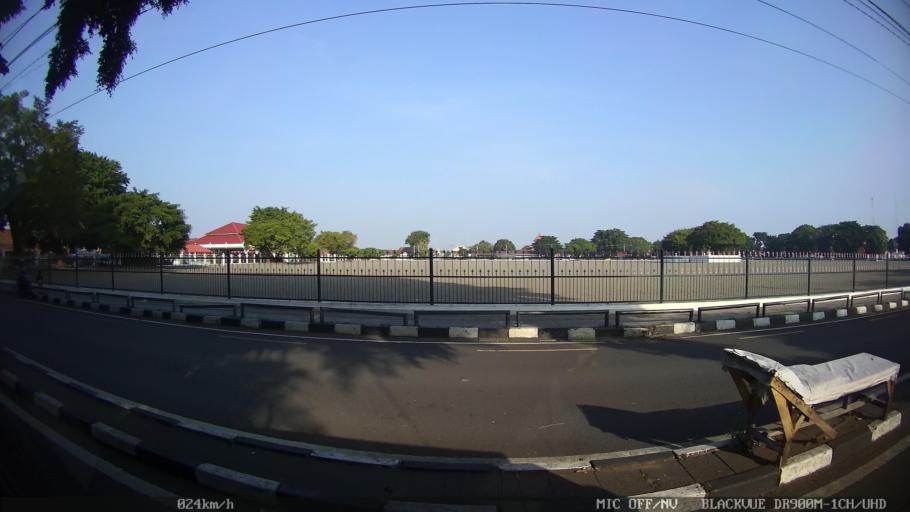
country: ID
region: Daerah Istimewa Yogyakarta
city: Yogyakarta
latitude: -7.8046
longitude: 110.3655
